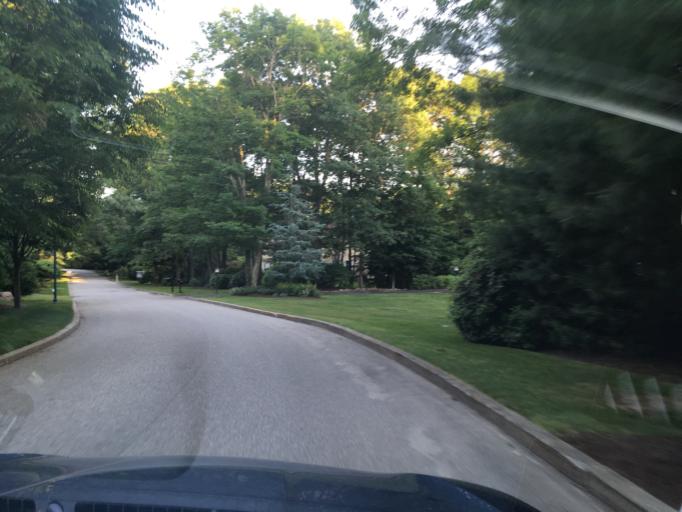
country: US
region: Rhode Island
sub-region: Washington County
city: Exeter
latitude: 41.6331
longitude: -71.5117
